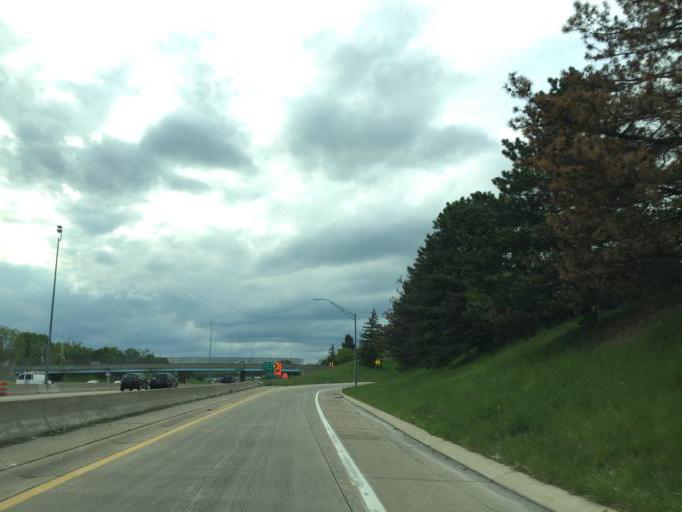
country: US
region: Michigan
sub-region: Wayne County
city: Dearborn Heights
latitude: 42.3810
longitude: -83.2369
